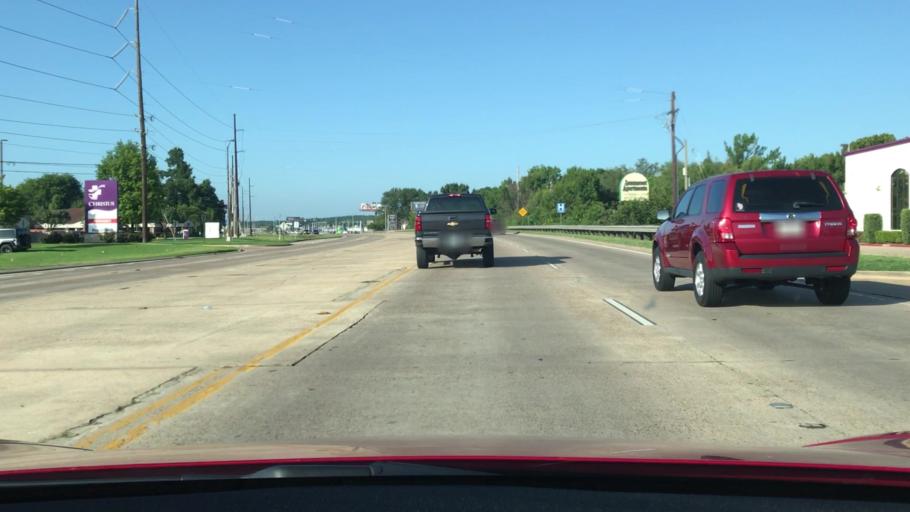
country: US
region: Louisiana
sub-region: Bossier Parish
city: Bossier City
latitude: 32.4269
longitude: -93.7183
